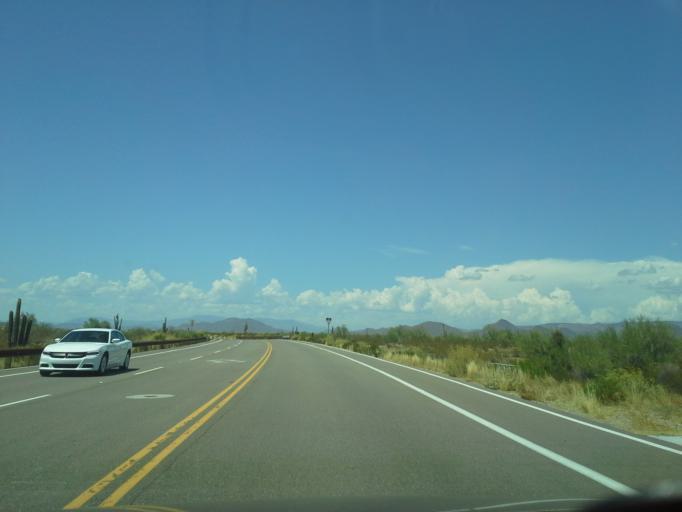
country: US
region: Arizona
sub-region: Maricopa County
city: Cave Creek
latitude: 33.7553
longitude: -112.0139
